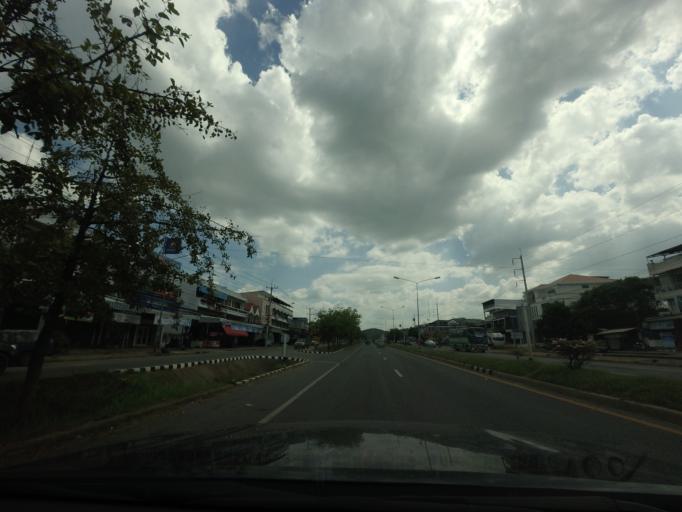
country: TH
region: Phetchabun
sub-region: Amphoe Bueng Sam Phan
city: Bueng Sam Phan
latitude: 15.7849
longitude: 101.0063
